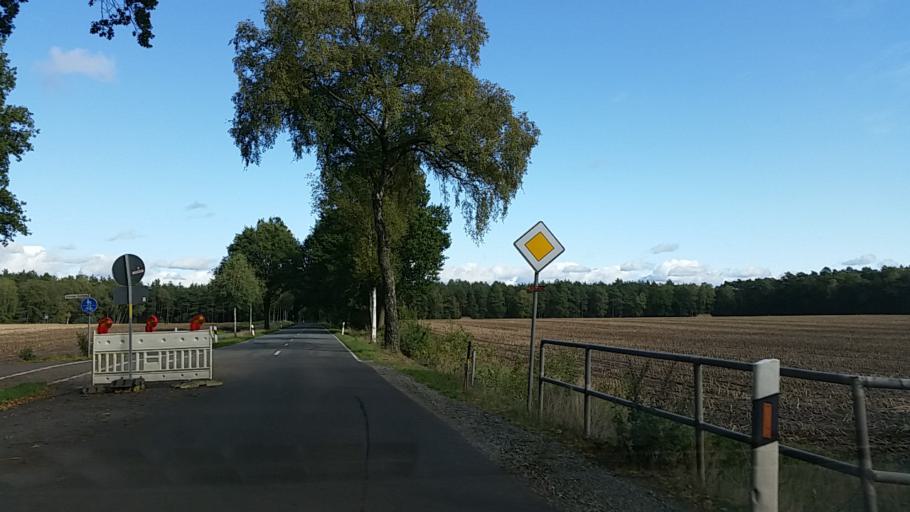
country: DE
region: Lower Saxony
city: Neuenkirchen
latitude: 53.0176
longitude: 9.6604
